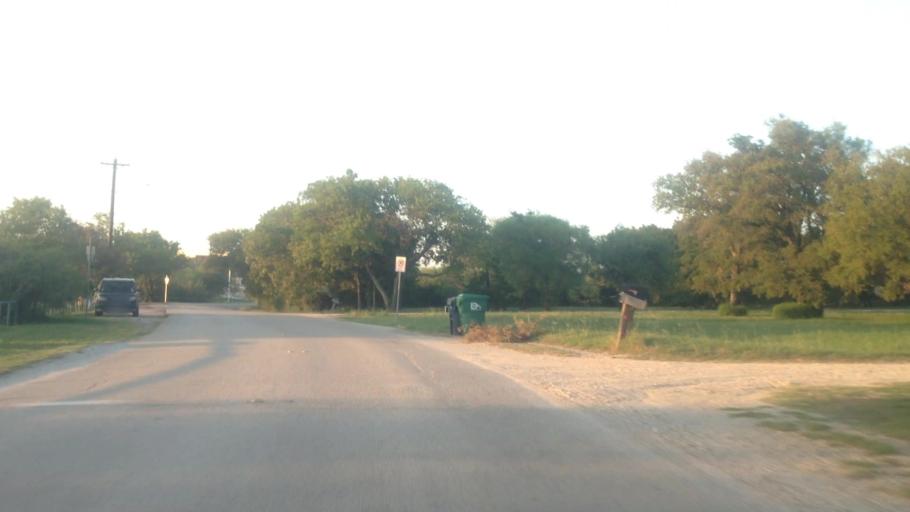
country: US
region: Texas
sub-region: Denton County
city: Denton
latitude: 33.2021
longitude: -97.1542
